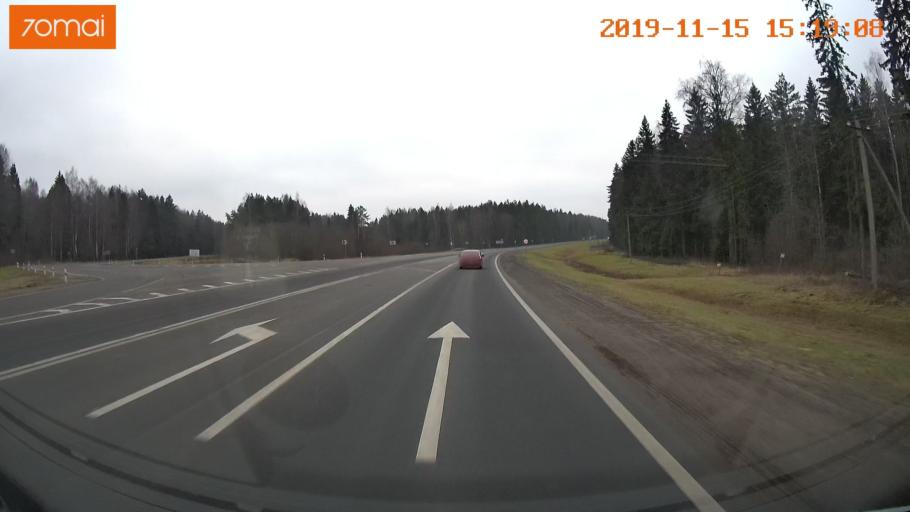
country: RU
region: Jaroslavl
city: Danilov
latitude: 58.2379
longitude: 40.1815
